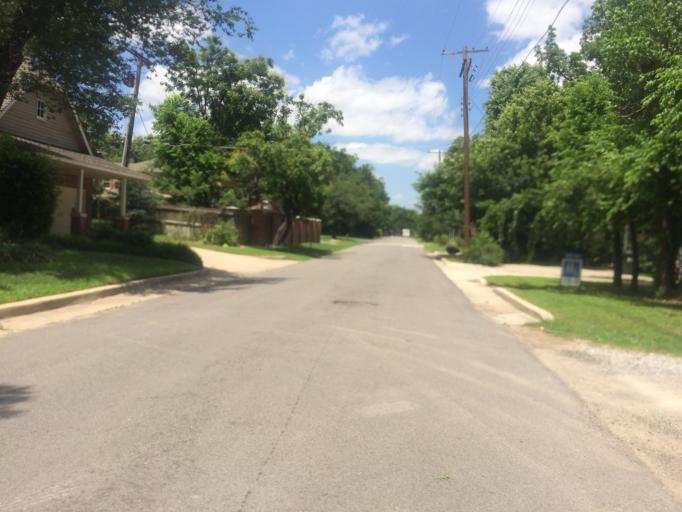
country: US
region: Oklahoma
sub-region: Cleveland County
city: Norman
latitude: 35.2085
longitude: -97.4325
